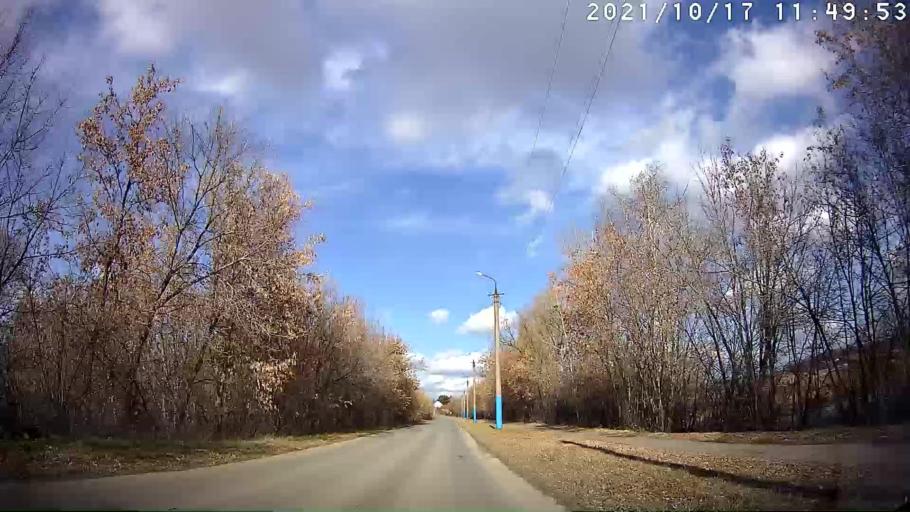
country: RU
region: Mariy-El
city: Kuzhener
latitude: 57.0088
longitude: 48.7371
